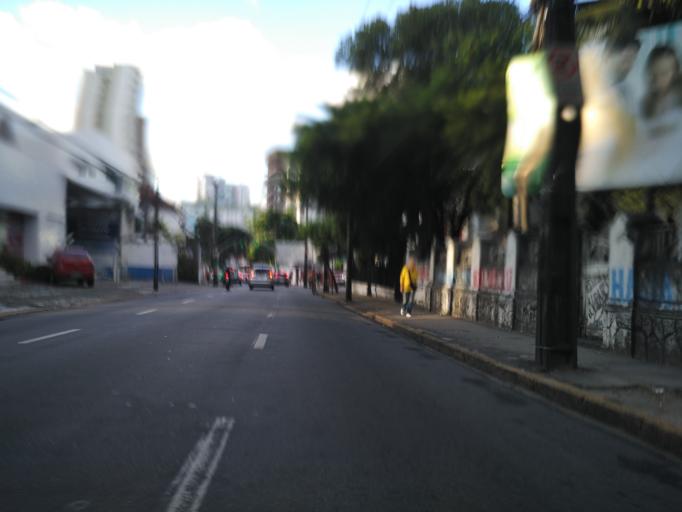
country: BR
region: Pernambuco
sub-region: Recife
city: Recife
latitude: -8.0428
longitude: -34.8977
